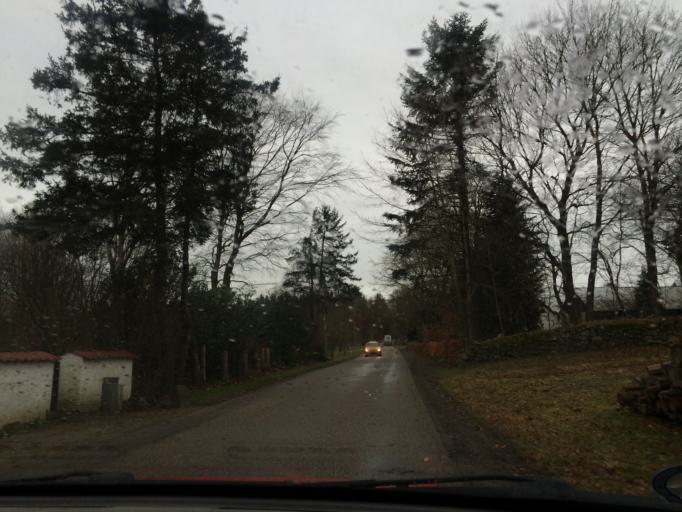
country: DK
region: Central Jutland
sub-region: Silkeborg Kommune
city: Virklund
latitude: 56.0262
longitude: 9.4641
